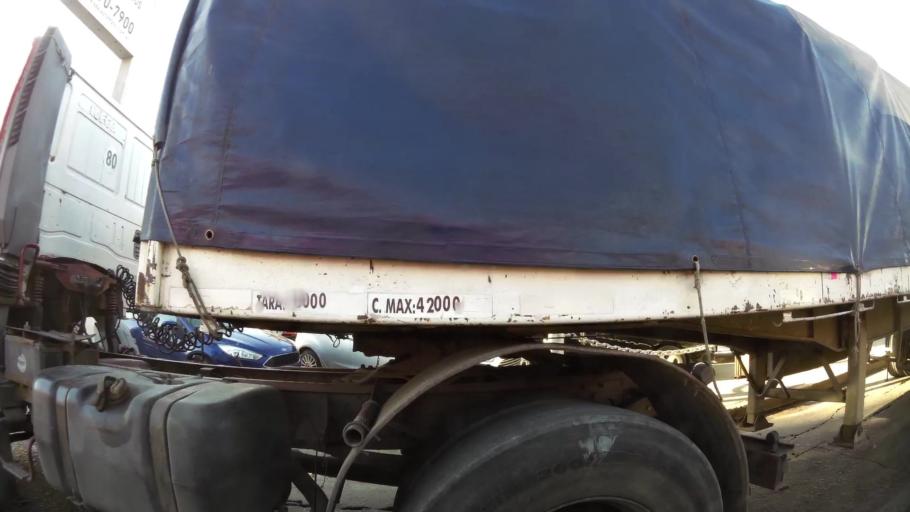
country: AR
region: Buenos Aires
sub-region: Partido de Almirante Brown
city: Adrogue
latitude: -34.7497
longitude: -58.3373
